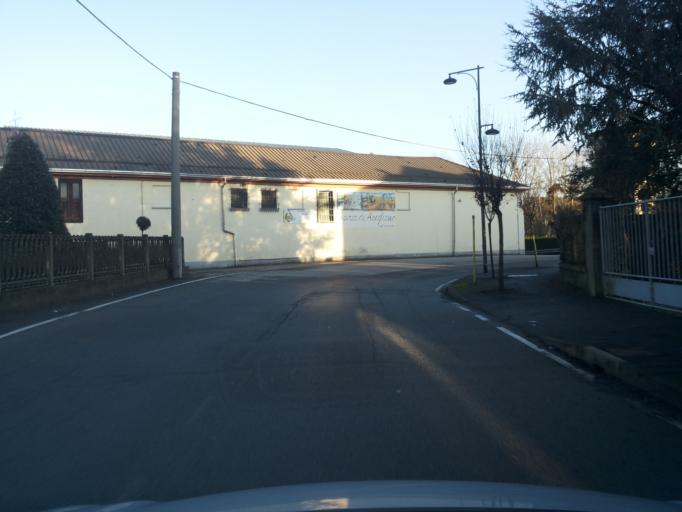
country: IT
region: Piedmont
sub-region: Provincia di Vercelli
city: Asigliano Vercellese
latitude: 45.2602
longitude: 8.4107
